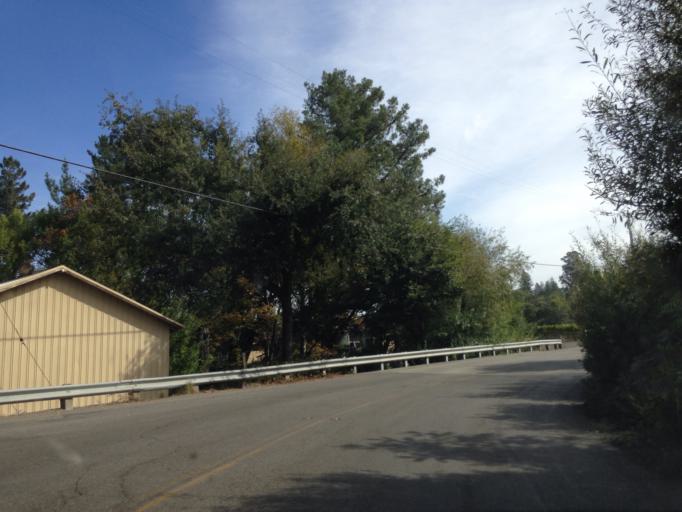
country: US
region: California
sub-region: Sonoma County
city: Graton
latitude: 38.4339
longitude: -122.8919
